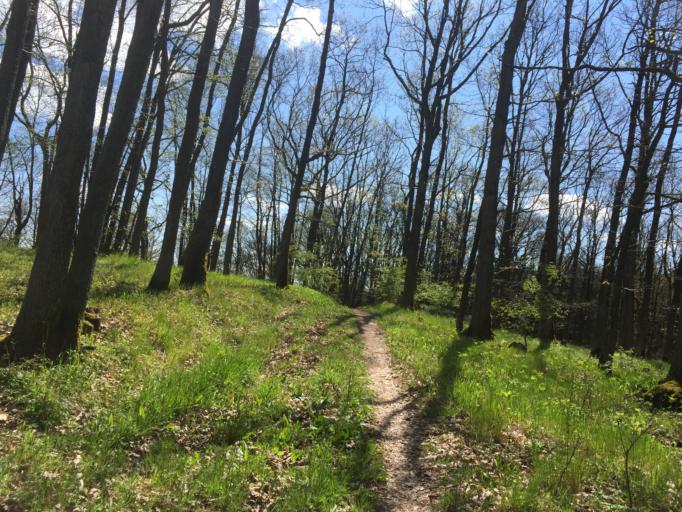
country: DE
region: Bavaria
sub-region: Regierungsbezirk Unterfranken
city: Sulzfeld
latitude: 50.2609
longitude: 10.4412
